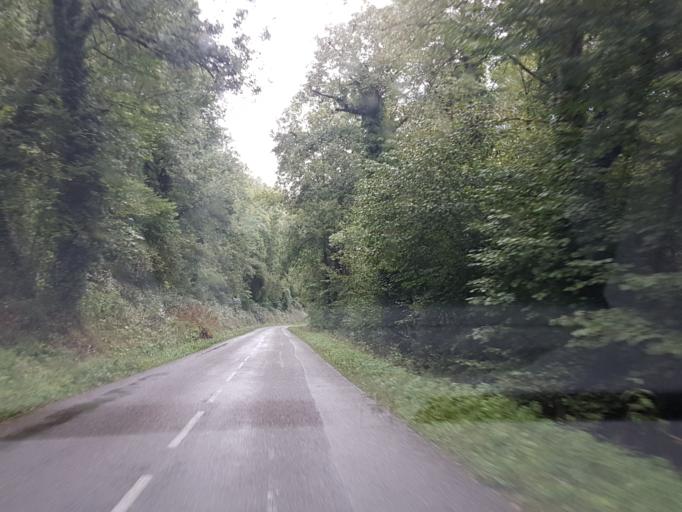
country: FR
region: Midi-Pyrenees
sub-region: Departement de l'Ariege
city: Saint-Girons
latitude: 42.9018
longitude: 1.2241
